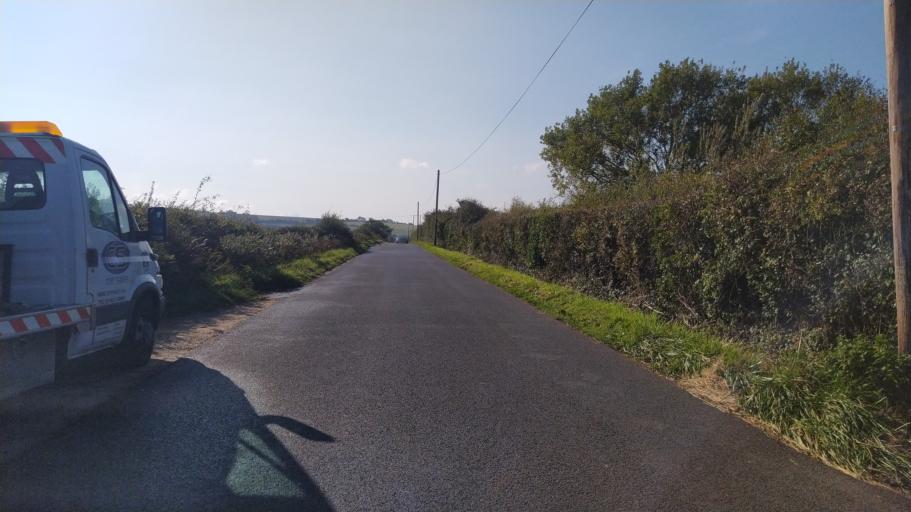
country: GB
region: England
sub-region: Isle of Wight
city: Northwood
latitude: 50.7018
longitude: -1.3458
